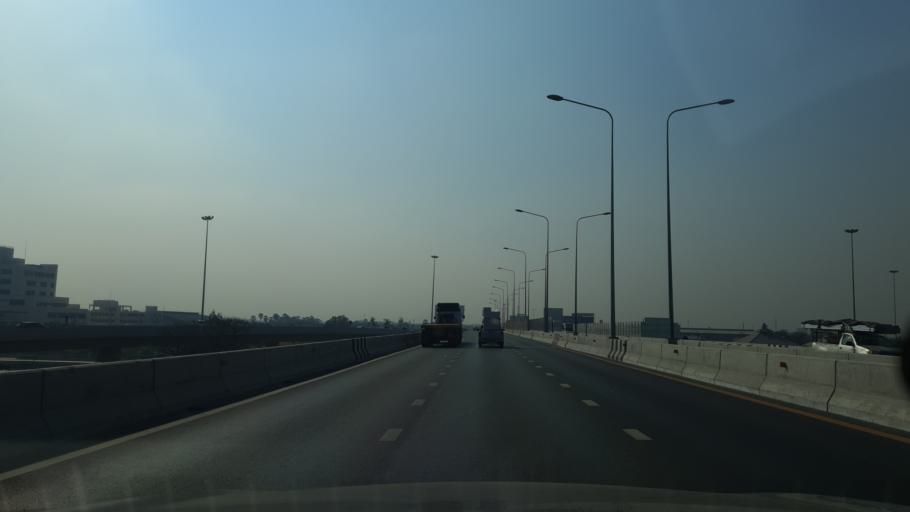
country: TH
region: Nonthaburi
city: Bang Bua Thong
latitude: 13.9519
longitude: 100.4588
